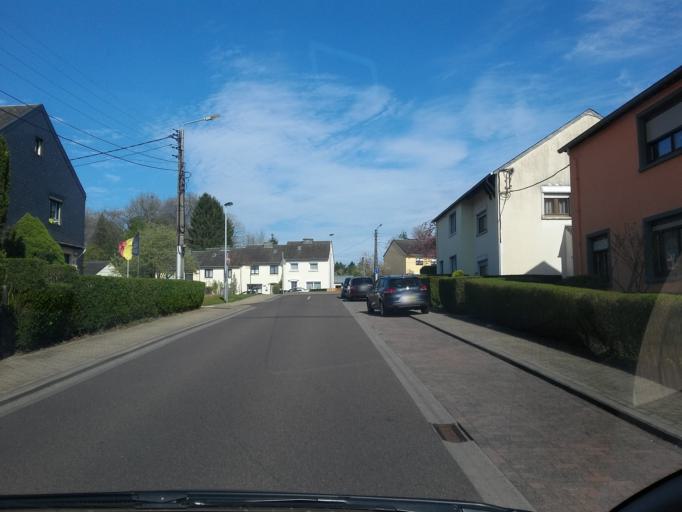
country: BE
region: Wallonia
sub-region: Province du Luxembourg
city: Arlon
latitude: 49.6839
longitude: 5.8030
